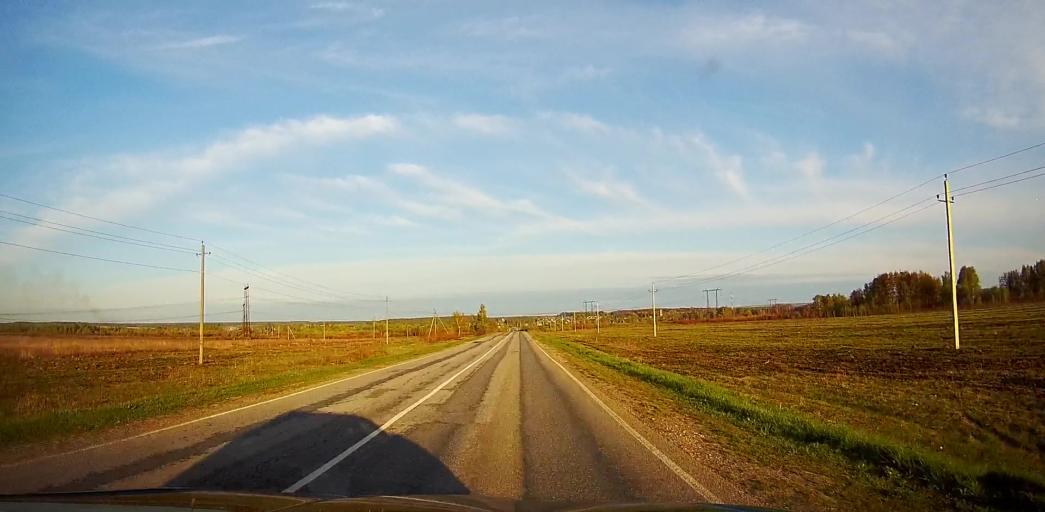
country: RU
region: Moskovskaya
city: Meshcherino
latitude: 55.2656
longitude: 38.2540
